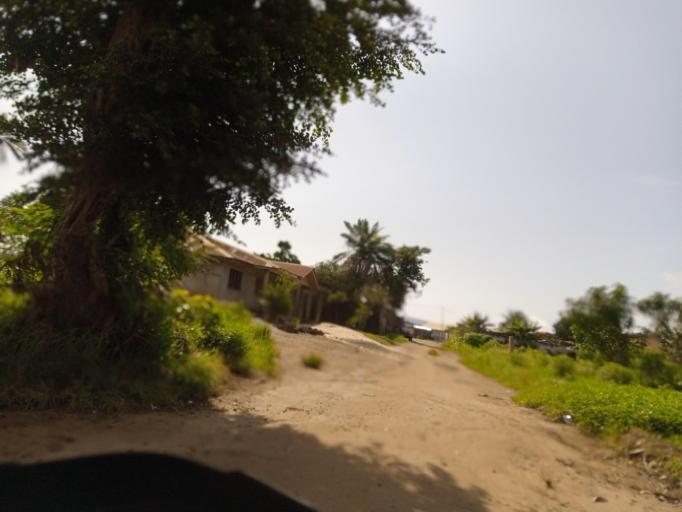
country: SL
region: Northern Province
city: Masoyila
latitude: 8.6102
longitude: -13.2045
